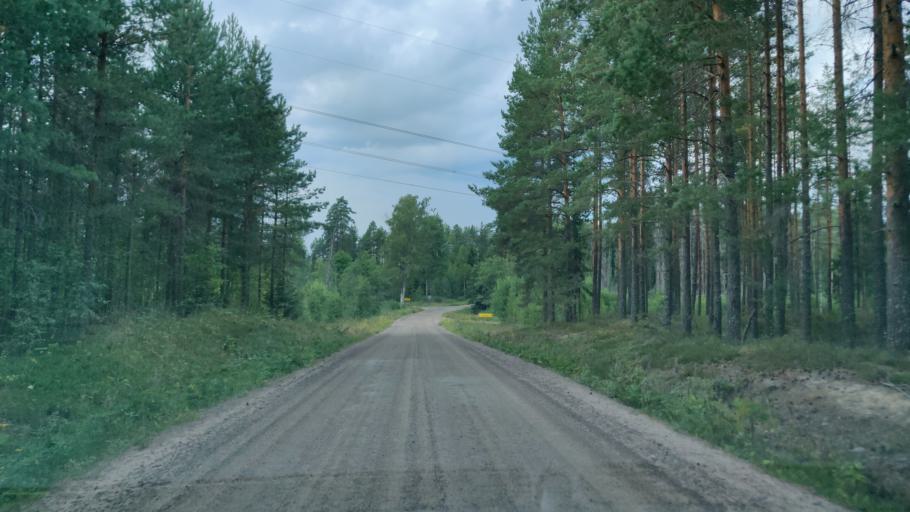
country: SE
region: Vaermland
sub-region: Munkfors Kommun
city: Munkfors
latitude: 59.9590
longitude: 13.4942
